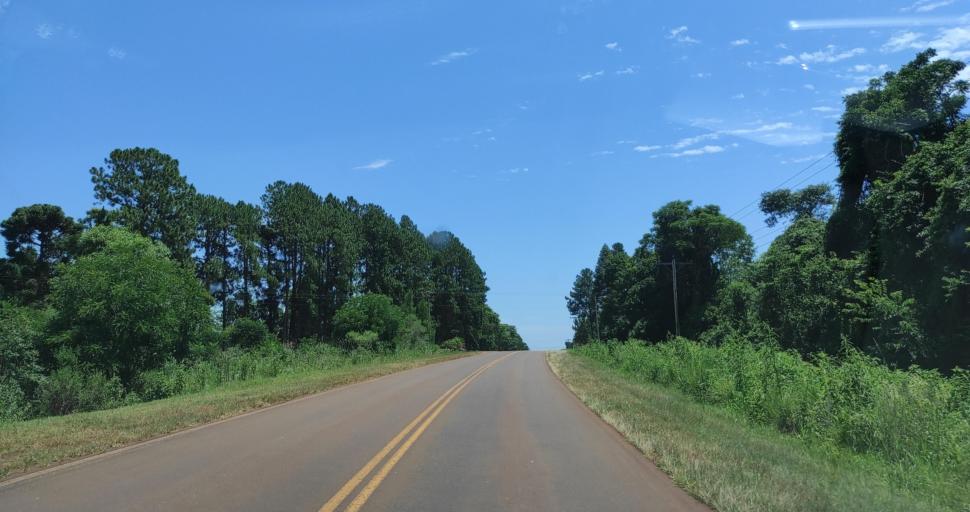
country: AR
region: Misiones
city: Ruiz de Montoya
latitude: -27.0026
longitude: -55.0426
